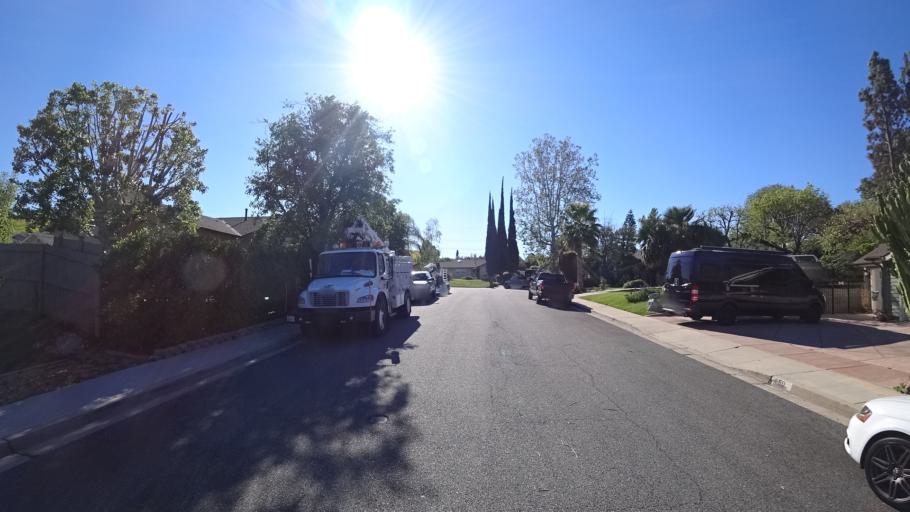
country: US
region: California
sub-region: Ventura County
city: Thousand Oaks
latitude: 34.1800
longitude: -118.8460
